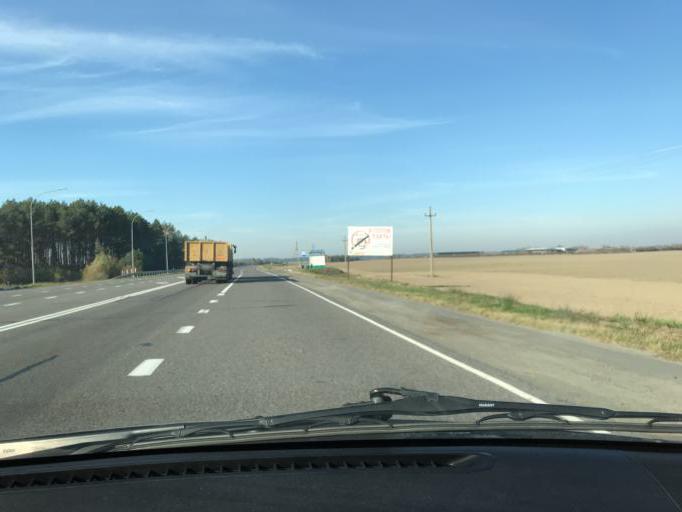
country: BY
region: Brest
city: Davyd-Haradok
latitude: 52.2480
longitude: 27.0831
